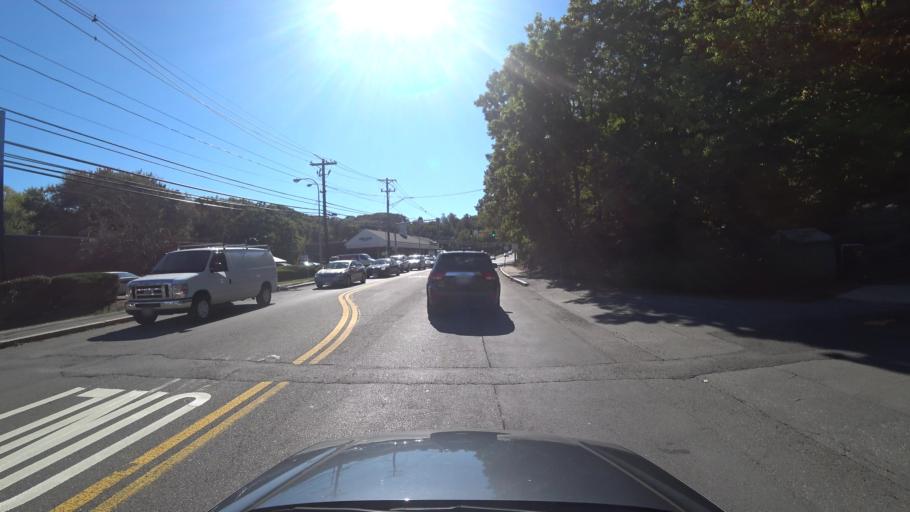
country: US
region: Massachusetts
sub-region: Essex County
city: Swampscott
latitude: 42.4806
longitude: -70.9039
